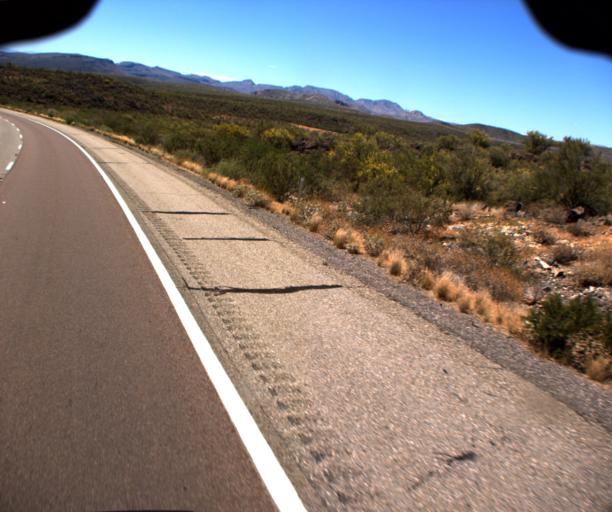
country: US
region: Arizona
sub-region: Yavapai County
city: Bagdad
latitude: 34.4997
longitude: -113.3975
